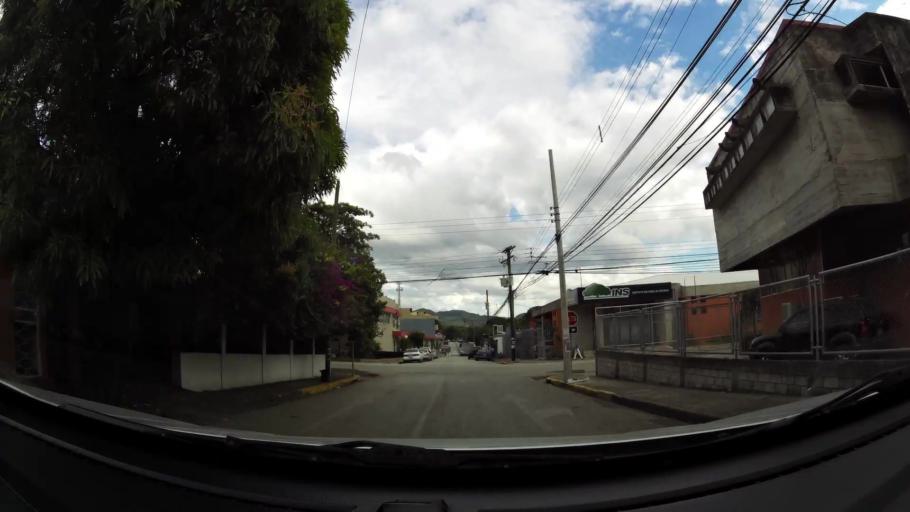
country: CR
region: Guanacaste
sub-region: Canton de Nicoya
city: Nicoya
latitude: 10.1452
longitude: -85.4531
